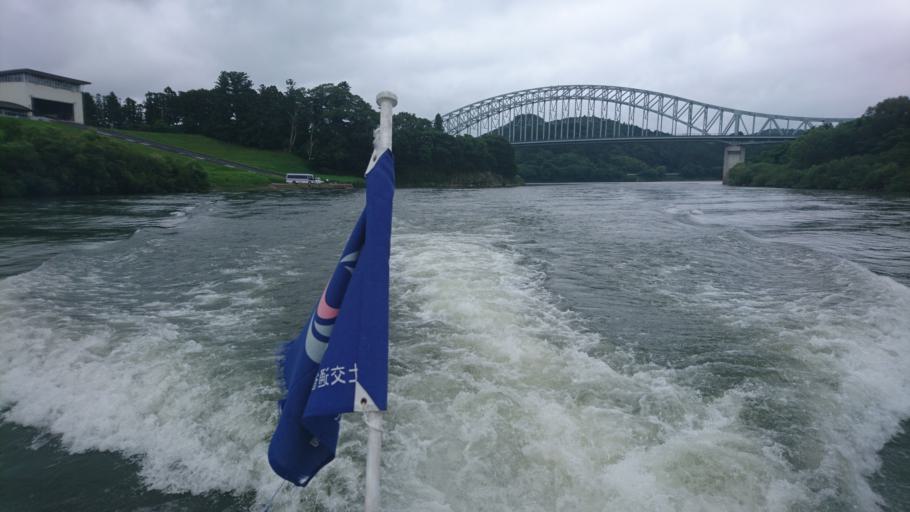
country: JP
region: Iwate
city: Ichinoseki
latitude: 38.9008
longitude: 141.2606
